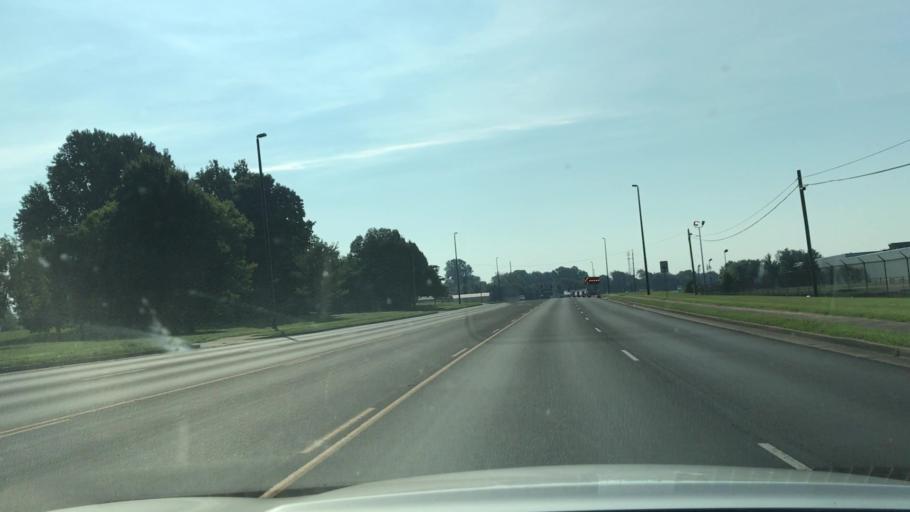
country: US
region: Kentucky
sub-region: Barren County
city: Glasgow
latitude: 37.0096
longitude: -85.9407
